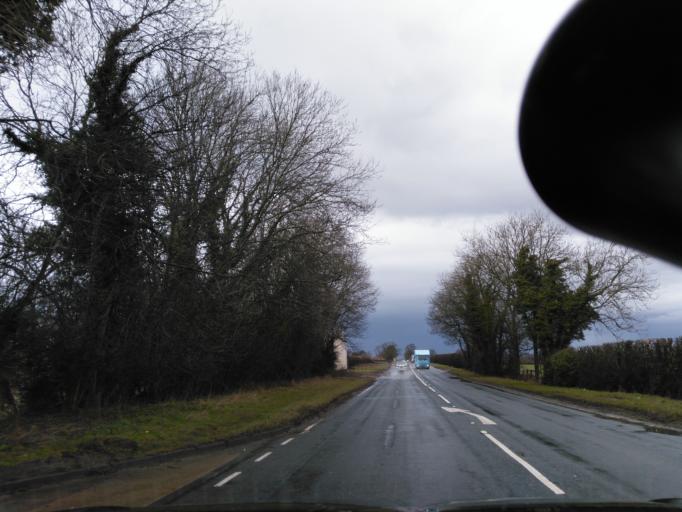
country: GB
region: England
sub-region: North Yorkshire
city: Ripon
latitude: 54.0844
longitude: -1.5300
